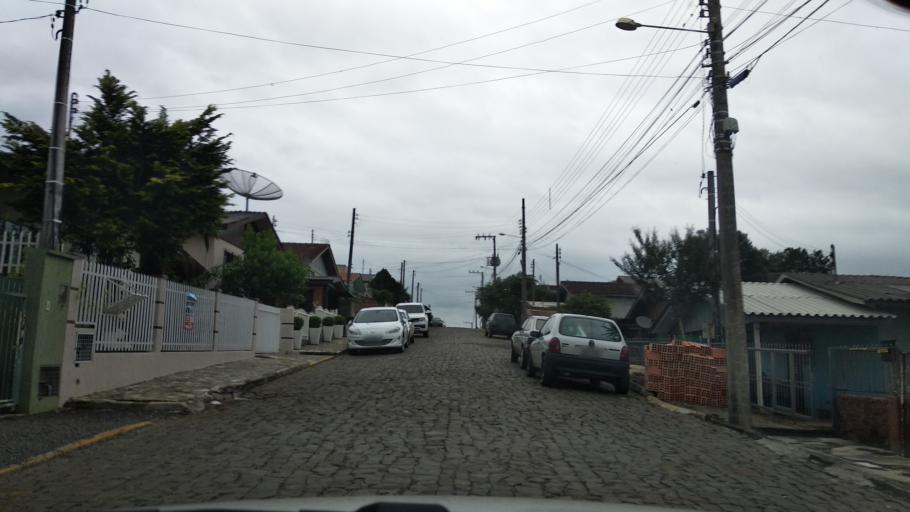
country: BR
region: Santa Catarina
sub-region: Videira
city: Videira
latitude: -26.9860
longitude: -51.1747
